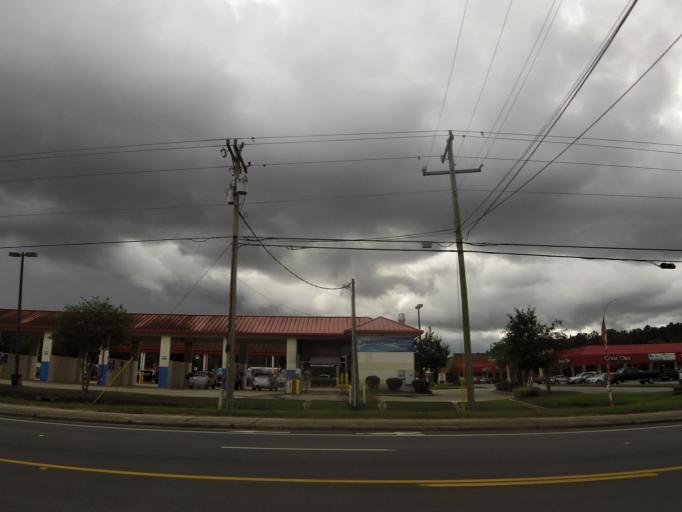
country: US
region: Florida
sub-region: Clay County
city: Middleburg
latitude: 30.0631
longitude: -81.8776
